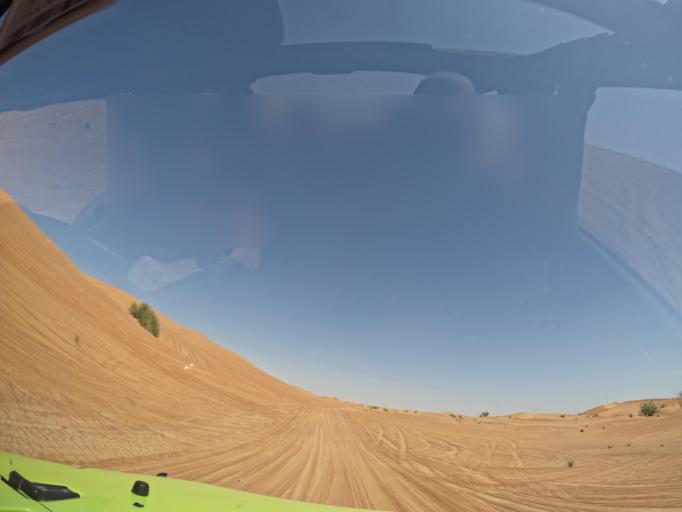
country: AE
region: Ash Shariqah
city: Adh Dhayd
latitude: 24.9953
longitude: 55.7250
